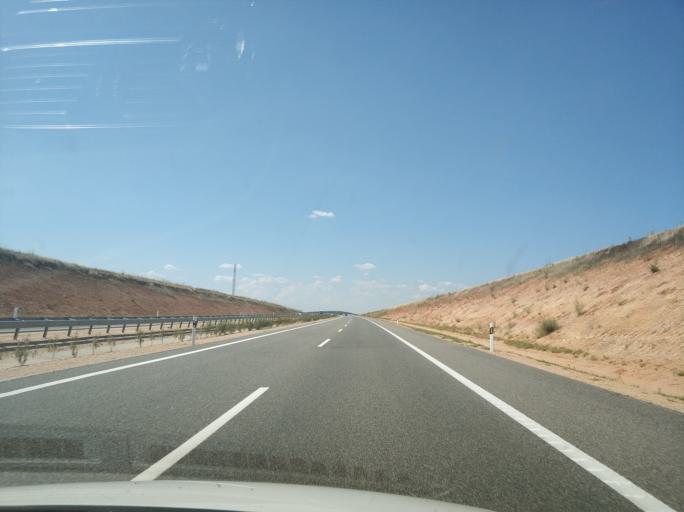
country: ES
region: Castille and Leon
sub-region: Provincia de Zamora
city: Montamarta
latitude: 41.6601
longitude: -5.7969
